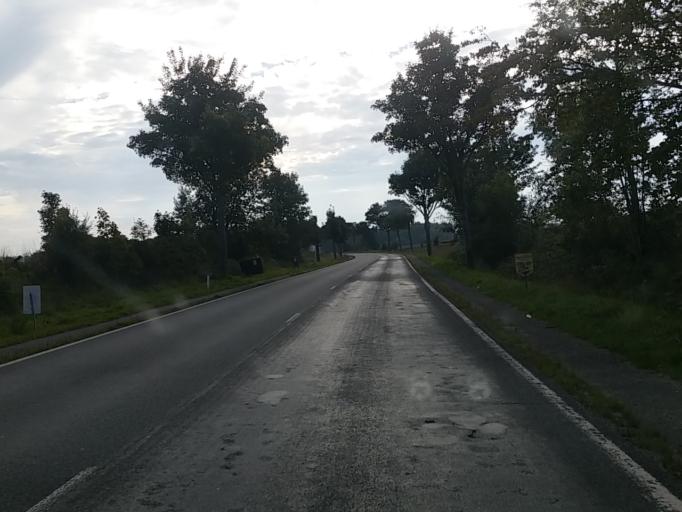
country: BE
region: Wallonia
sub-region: Province du Luxembourg
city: Florenville
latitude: 49.6954
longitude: 5.3220
